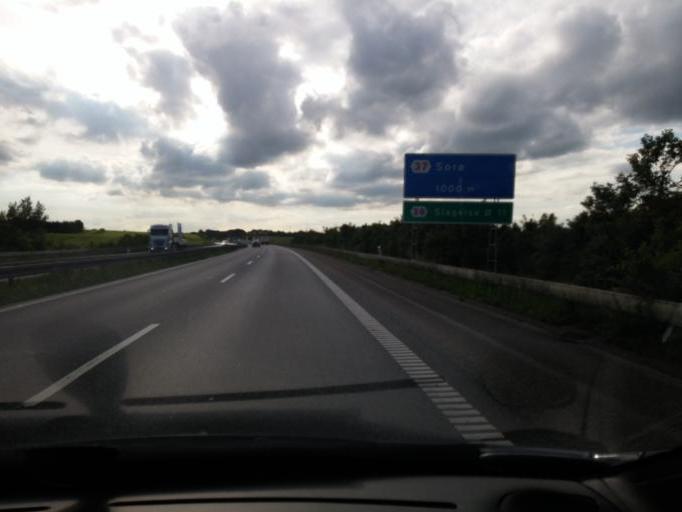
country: DK
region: Zealand
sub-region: Soro Kommune
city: Soro
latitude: 55.4596
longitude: 11.5825
